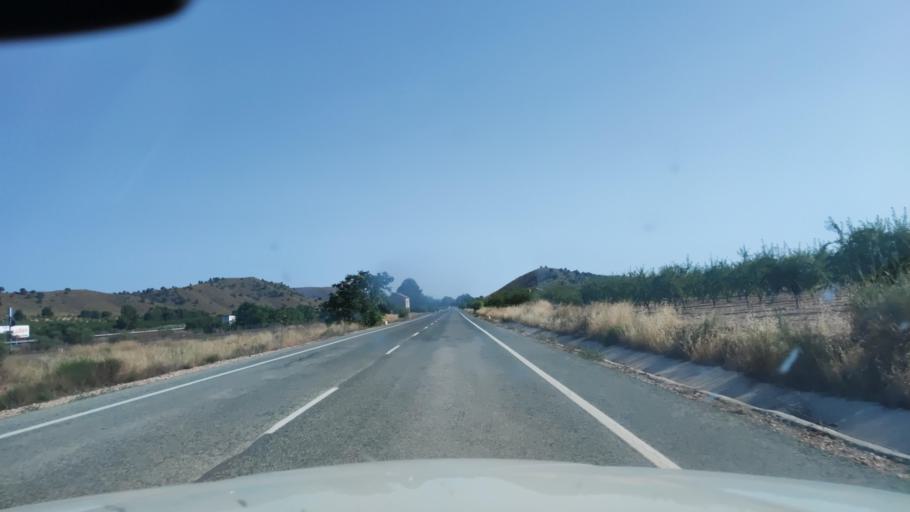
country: ES
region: Castille-La Mancha
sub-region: Provincia de Albacete
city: Tobarra
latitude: 38.6519
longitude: -1.6644
